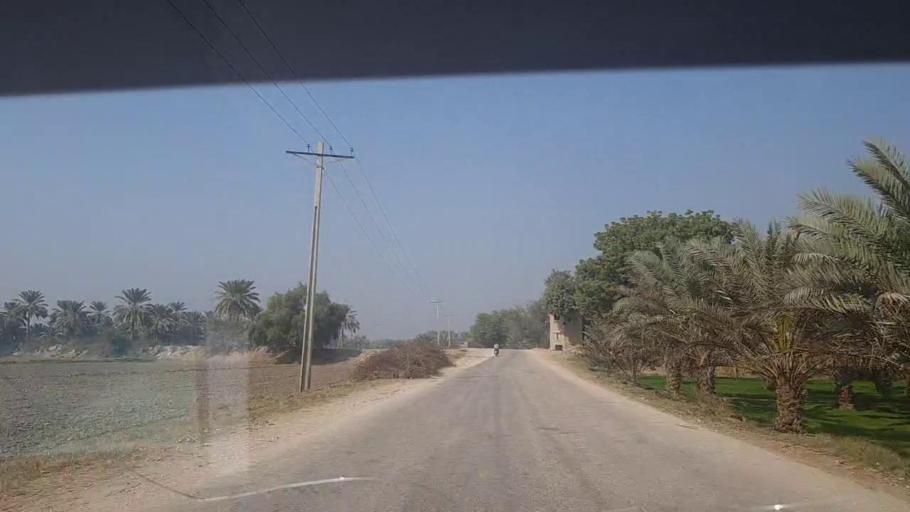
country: PK
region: Sindh
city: Kot Diji
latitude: 27.3701
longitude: 68.7007
